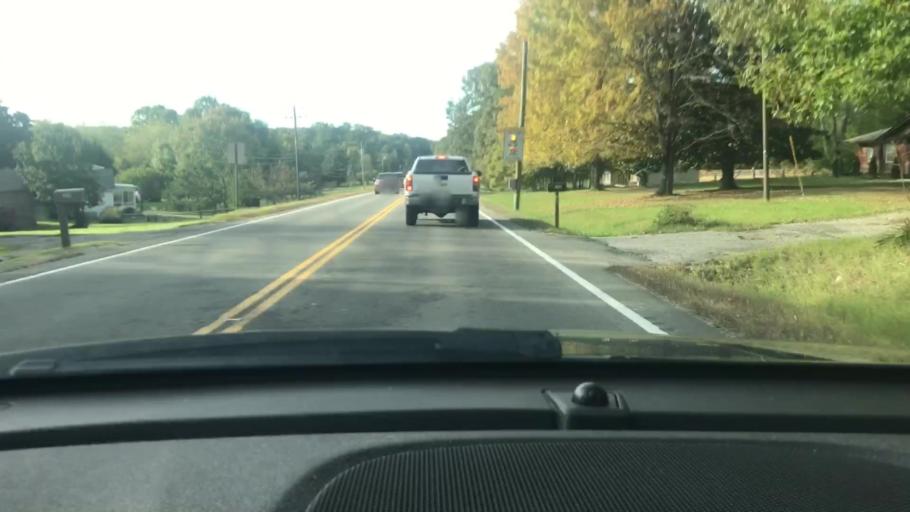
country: US
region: Tennessee
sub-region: Williamson County
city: Fairview
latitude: 35.9888
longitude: -87.1217
